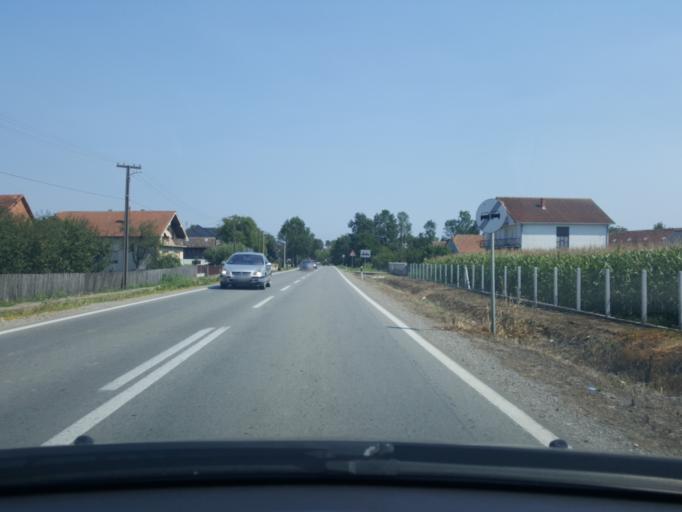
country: RS
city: Bogosavac
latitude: 44.7543
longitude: 19.5481
